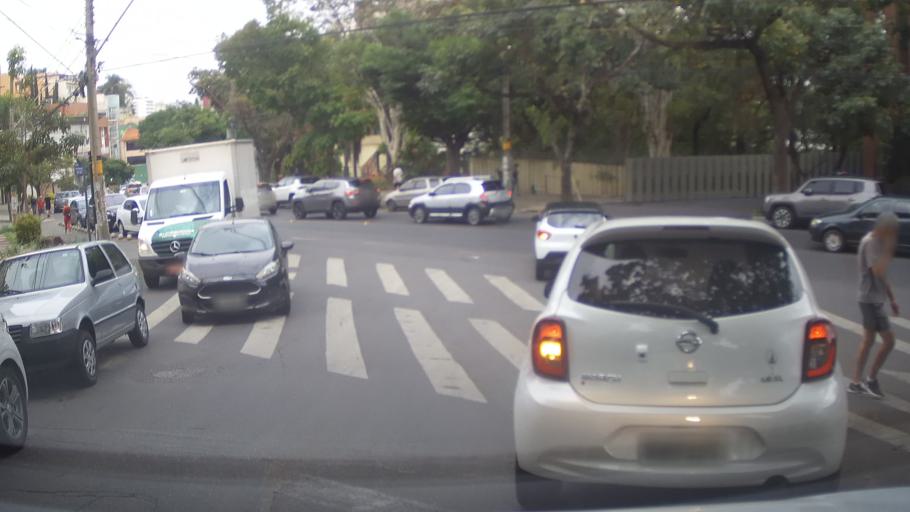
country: BR
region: Minas Gerais
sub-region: Belo Horizonte
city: Belo Horizonte
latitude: -19.9541
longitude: -43.9260
